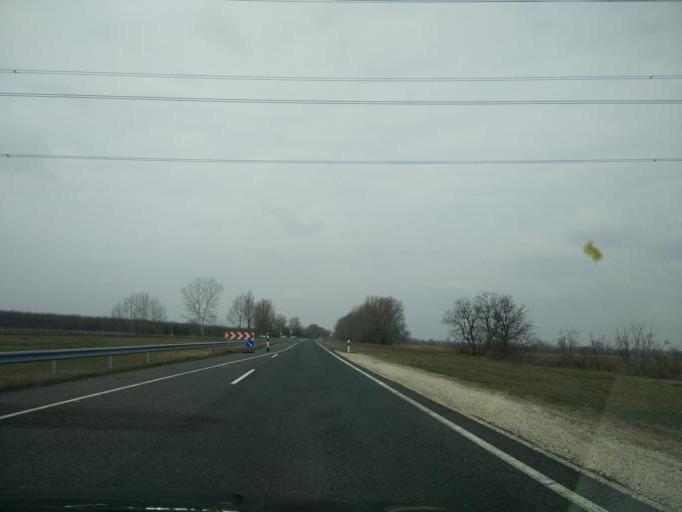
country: HU
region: Gyor-Moson-Sopron
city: Per
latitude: 47.6889
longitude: 17.8025
